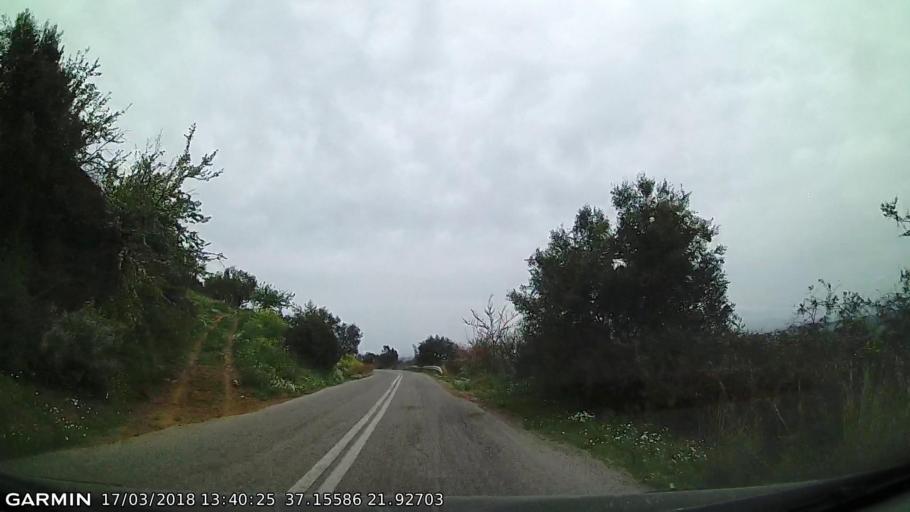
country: GR
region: Peloponnese
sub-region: Nomos Messinias
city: Meligalas
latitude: 37.1557
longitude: 21.9271
